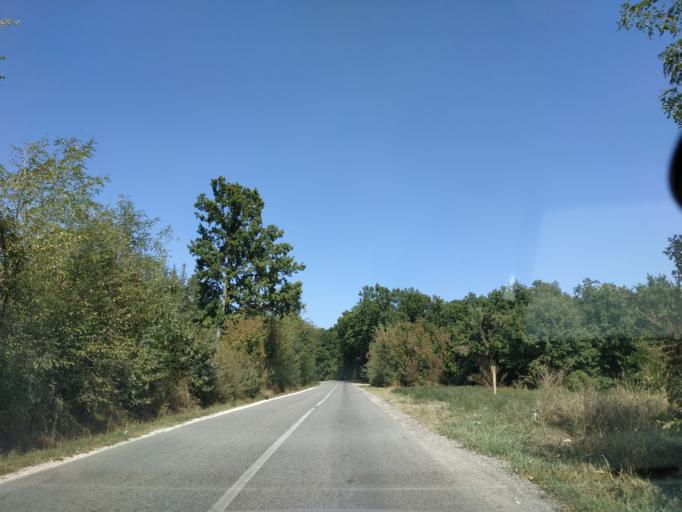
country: RS
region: Central Serbia
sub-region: Sumadijski Okrug
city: Arangelovac
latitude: 44.2855
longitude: 20.6098
